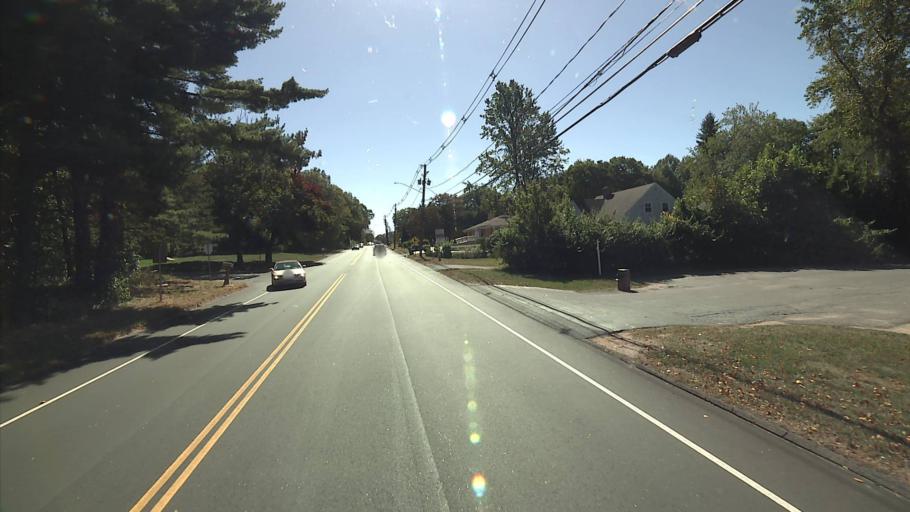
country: US
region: Connecticut
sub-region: New Haven County
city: Prospect
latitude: 41.5166
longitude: -72.9880
